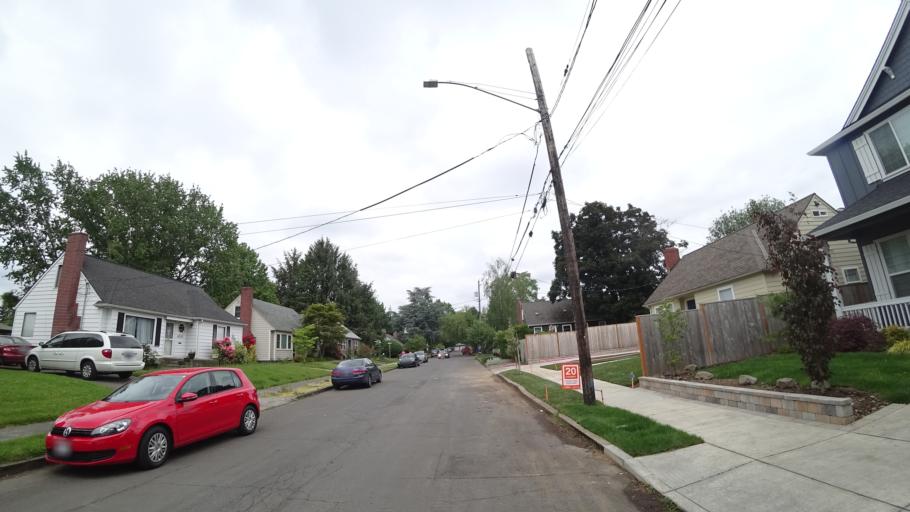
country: US
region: Oregon
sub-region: Clackamas County
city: Milwaukie
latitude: 45.4886
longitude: -122.6283
